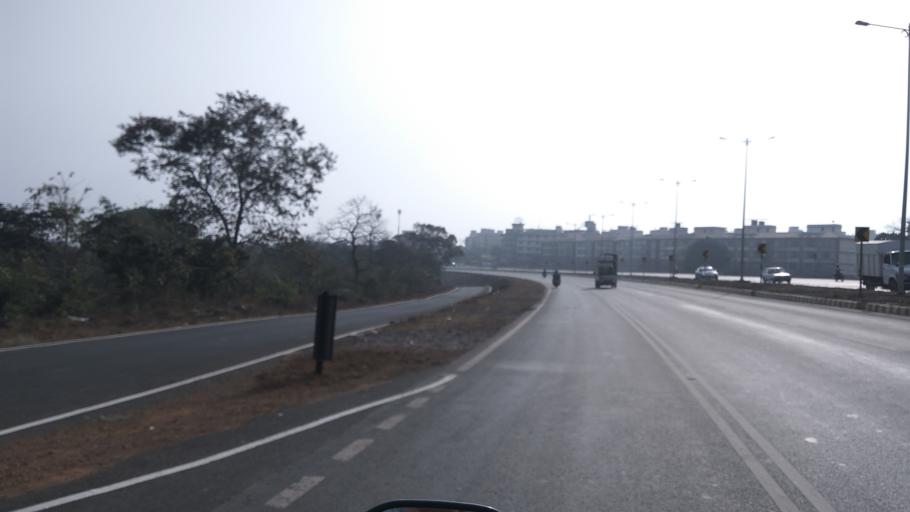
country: IN
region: Goa
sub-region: North Goa
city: Goa Velha
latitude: 15.4869
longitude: 73.8997
